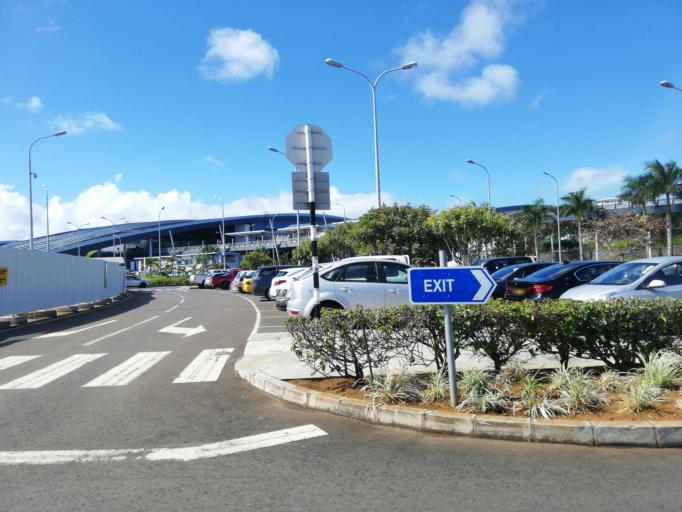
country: MU
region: Grand Port
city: Plaine Magnien
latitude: -20.4350
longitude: 57.6776
